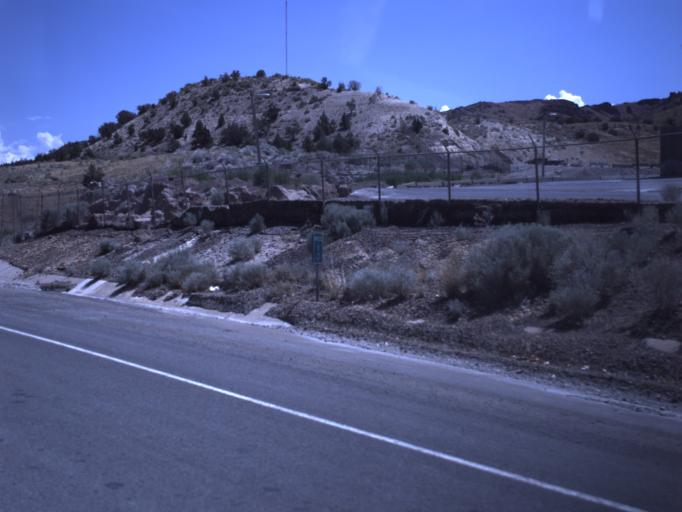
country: US
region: Utah
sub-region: Juab County
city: Nephi
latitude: 39.5650
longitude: -112.1971
